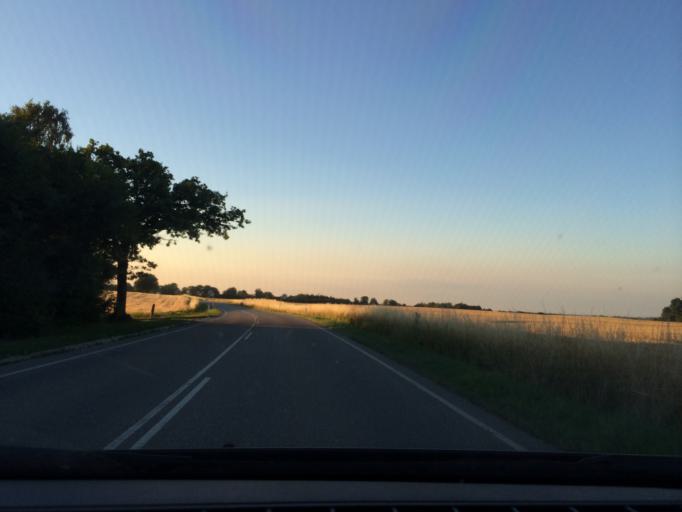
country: DK
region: Zealand
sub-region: Vordingborg Kommune
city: Praesto
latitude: 55.0842
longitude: 12.0826
